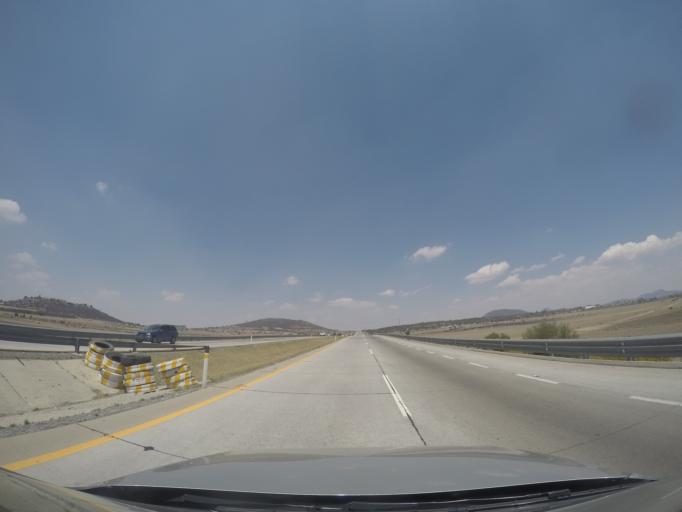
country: MX
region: Morelos
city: Jaltepec
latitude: 19.7632
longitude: -98.6333
